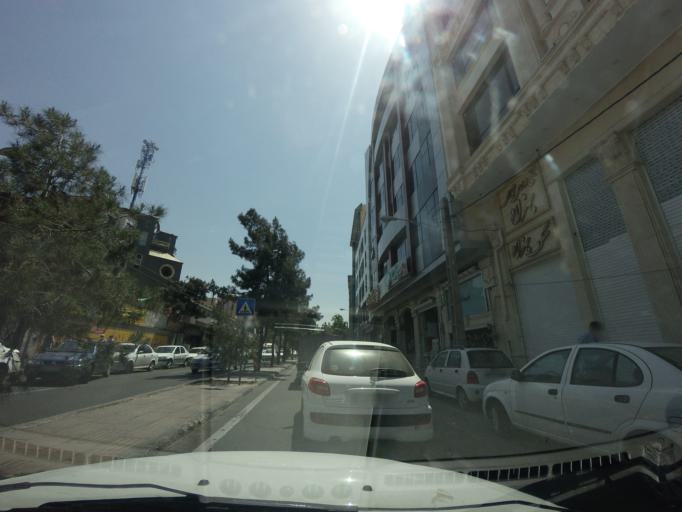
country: IR
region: Tehran
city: Tehran
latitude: 35.7247
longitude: 51.3115
